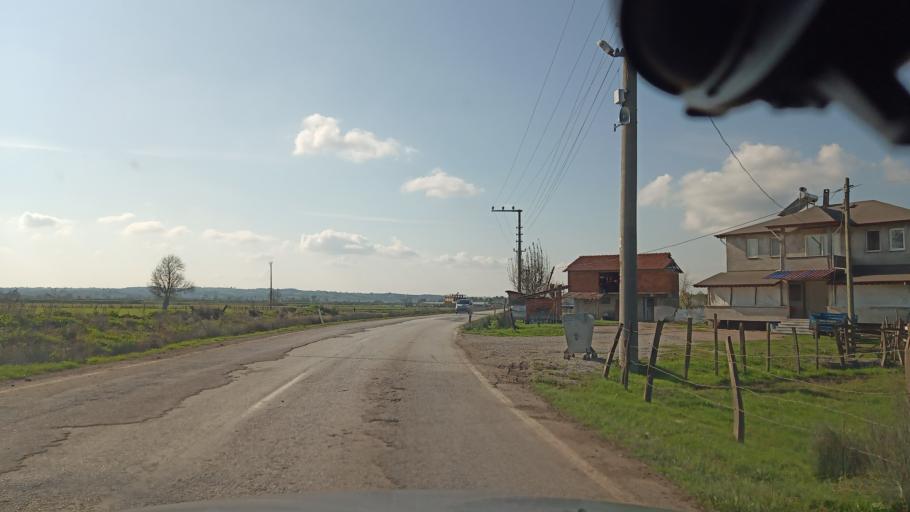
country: TR
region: Sakarya
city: Kaynarca
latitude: 41.0965
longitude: 30.4321
